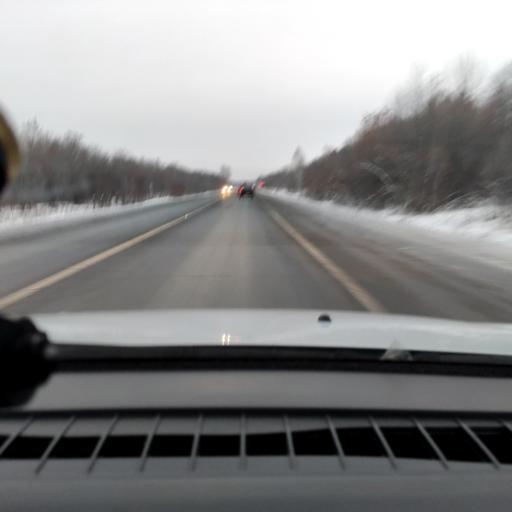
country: RU
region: Samara
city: Chapayevsk
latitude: 52.9947
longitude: 49.8122
